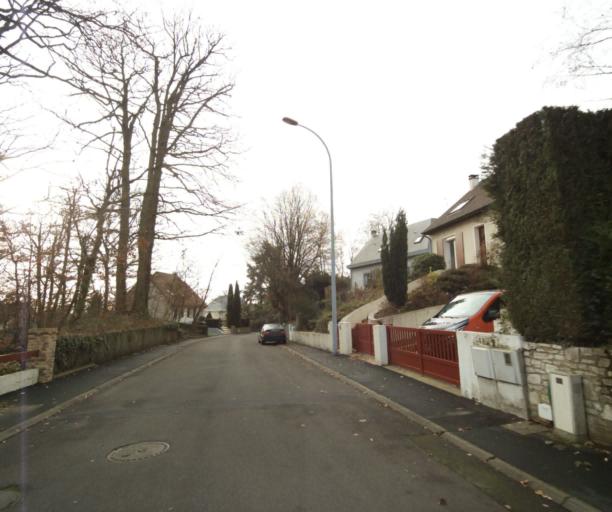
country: FR
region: Pays de la Loire
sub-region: Departement de la Sarthe
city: Le Mans
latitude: 48.0036
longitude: 0.2238
